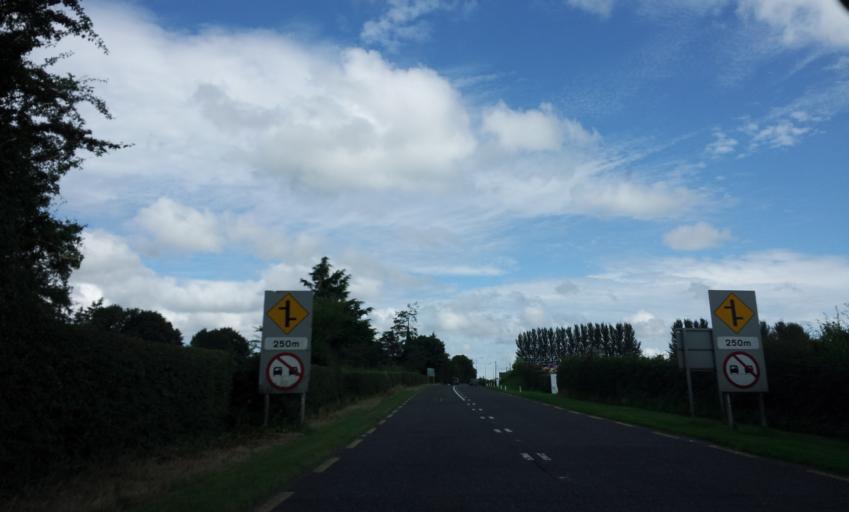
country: IE
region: Leinster
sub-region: Laois
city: Mountrath
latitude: 52.9835
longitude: -7.4916
